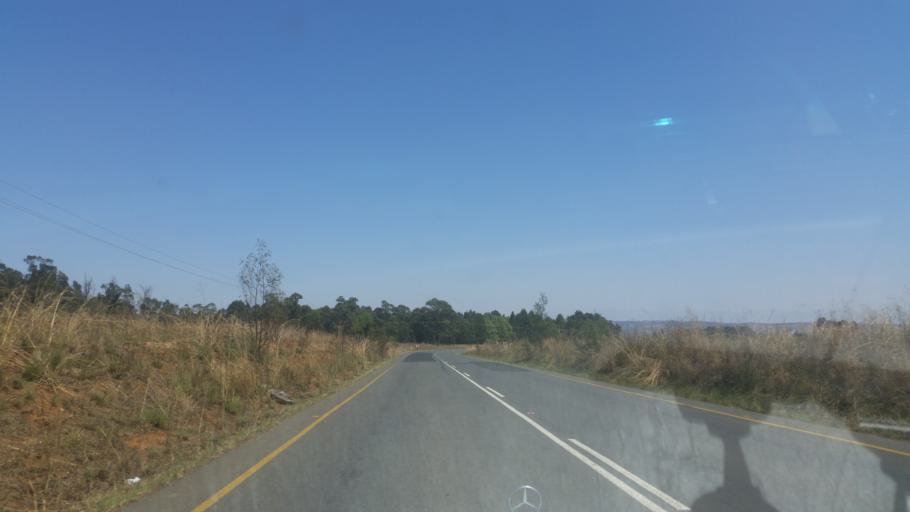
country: ZA
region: KwaZulu-Natal
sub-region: uMgungundlovu District Municipality
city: Mooirivier
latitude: -29.1479
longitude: 29.9872
